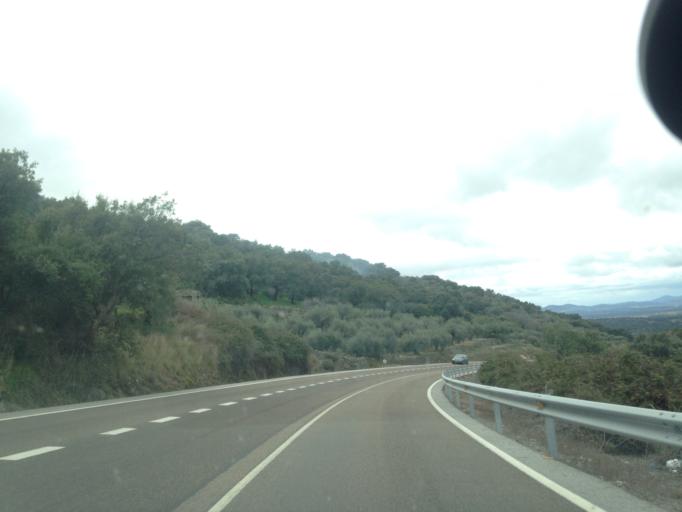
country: ES
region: Extremadura
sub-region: Provincia de Caceres
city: Montanchez
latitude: 39.2319
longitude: -6.1543
